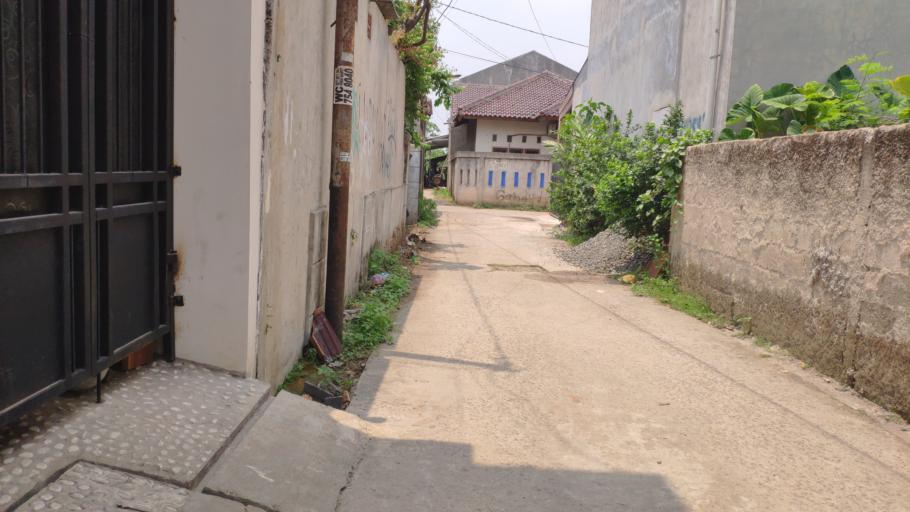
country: ID
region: West Java
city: Pamulang
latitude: -6.3315
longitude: 106.7935
